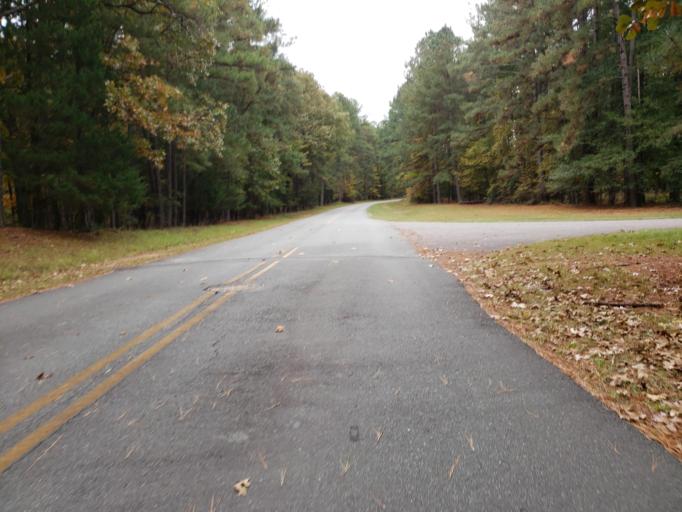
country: US
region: North Carolina
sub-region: Chatham County
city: Fearrington Village
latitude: 35.7598
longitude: -79.0444
